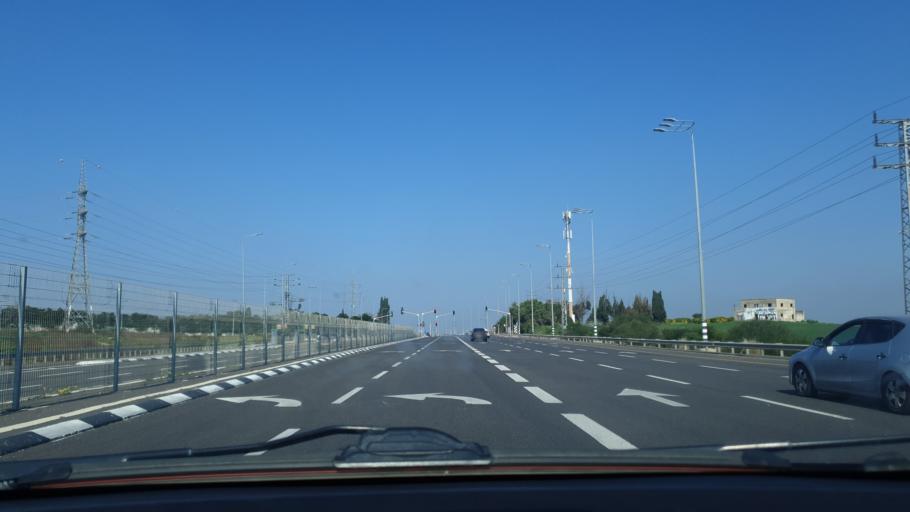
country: IL
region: Central District
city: Kefar Habad
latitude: 31.9726
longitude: 34.8413
